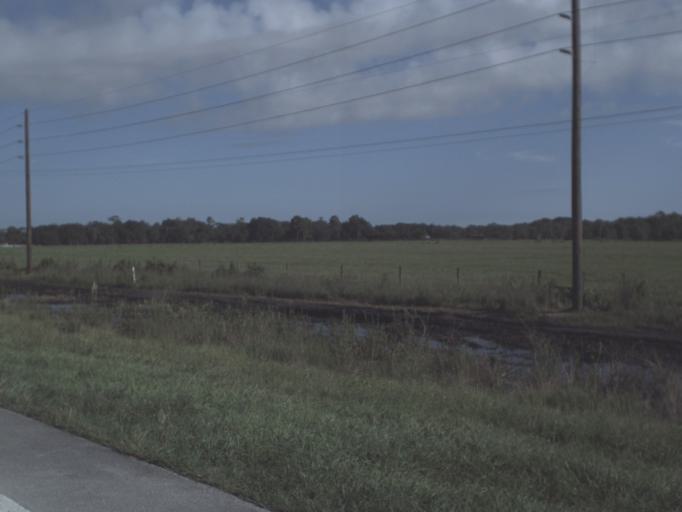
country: US
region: Florida
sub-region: Indian River County
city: Fellsmere
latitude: 27.5896
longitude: -80.8412
